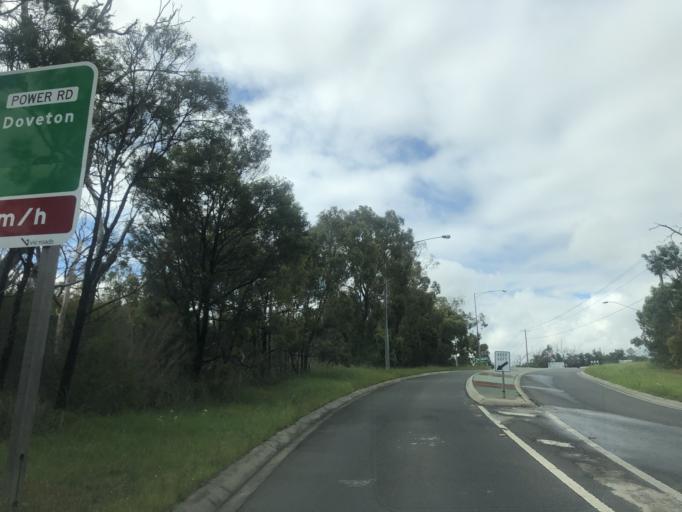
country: AU
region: Victoria
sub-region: Knox
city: Rowville
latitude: -37.9438
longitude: 145.2439
